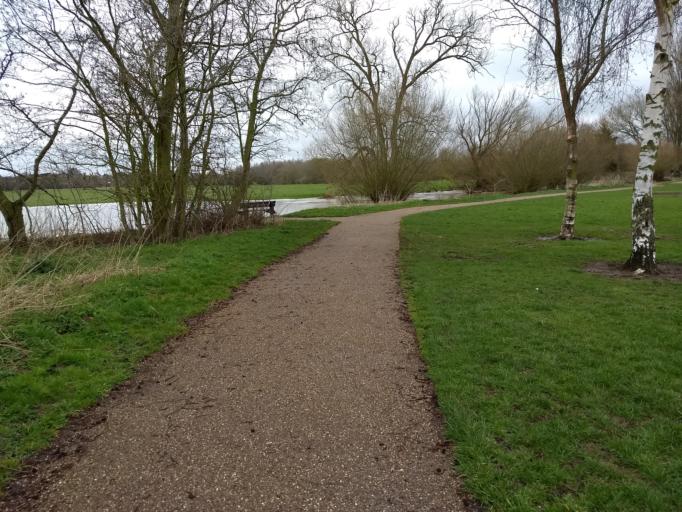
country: GB
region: England
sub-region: Milton Keynes
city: Stony Stratford
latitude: 52.0554
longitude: -0.8608
